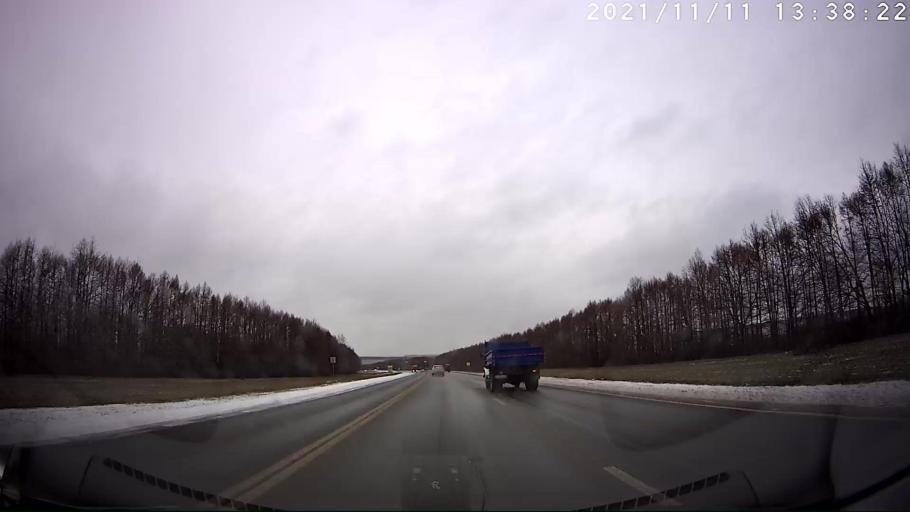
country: RU
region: Chuvashia
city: Kanash
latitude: 55.4292
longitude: 47.5270
